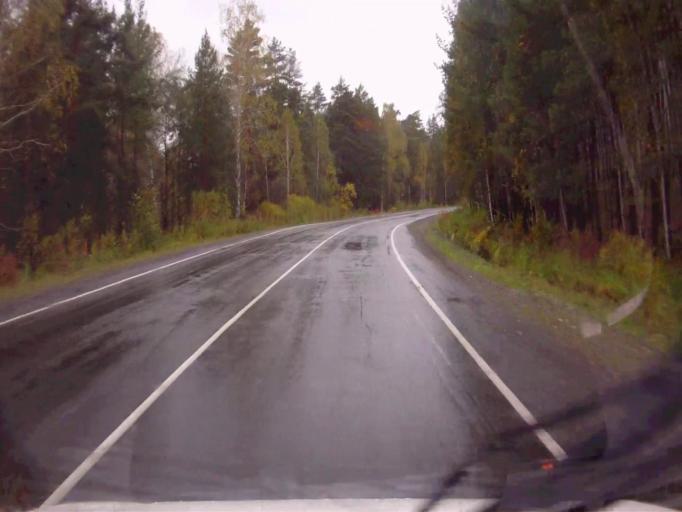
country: RU
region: Chelyabinsk
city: Verkhniy Ufaley
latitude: 55.9596
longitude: 60.3835
